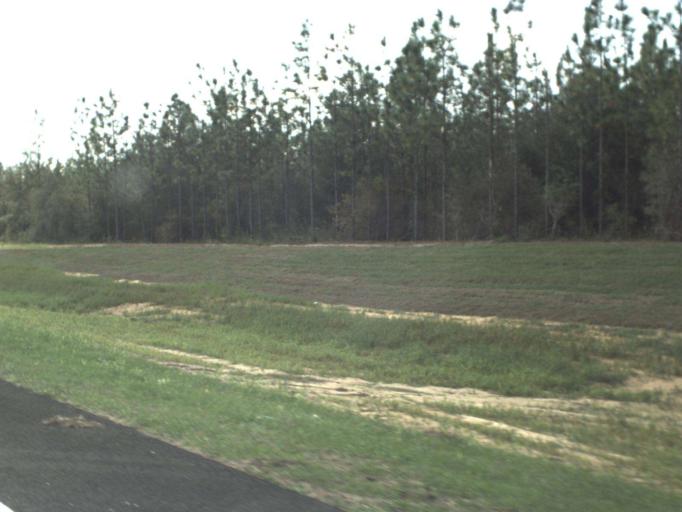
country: US
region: Florida
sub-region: Holmes County
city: Bonifay
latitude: 30.5622
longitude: -85.8116
